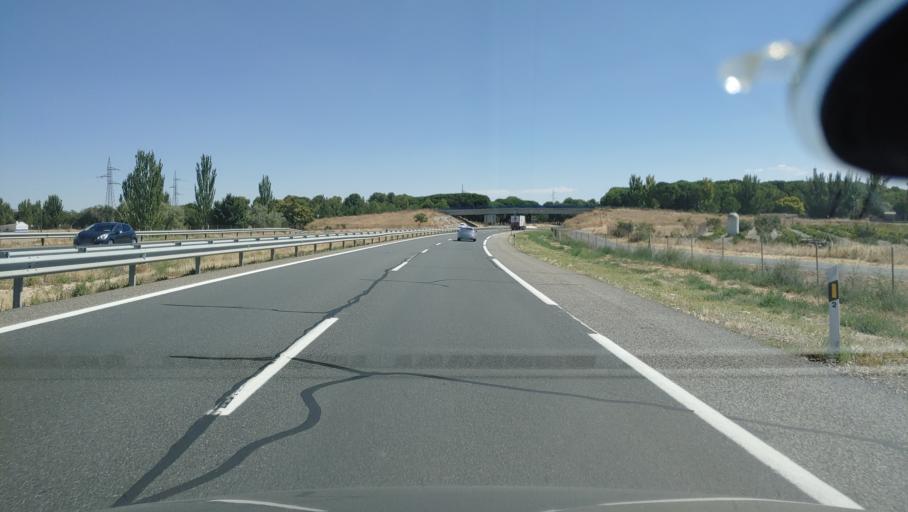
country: ES
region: Castille-La Mancha
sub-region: Provincia de Ciudad Real
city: Villarta de San Juan
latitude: 39.2446
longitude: -3.4178
